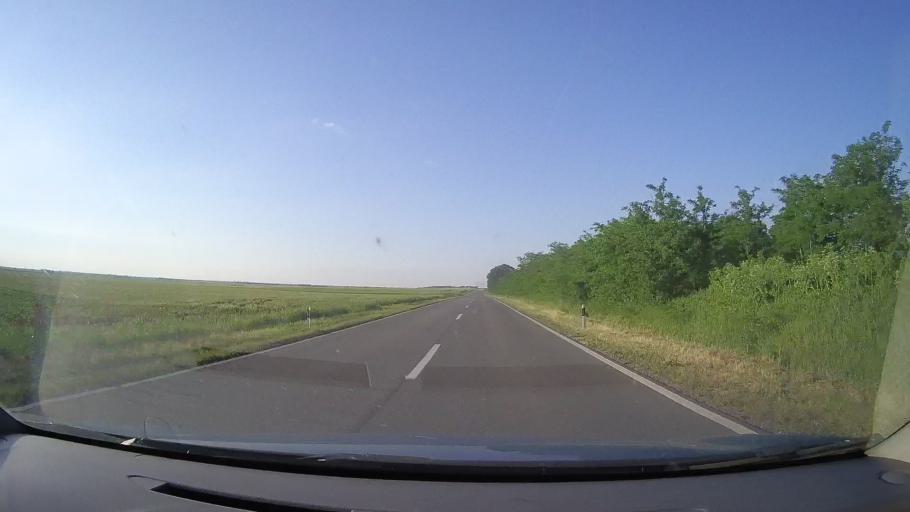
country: RS
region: Autonomna Pokrajina Vojvodina
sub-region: Juznobanatski Okrug
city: Vrsac
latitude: 45.1833
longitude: 21.2965
